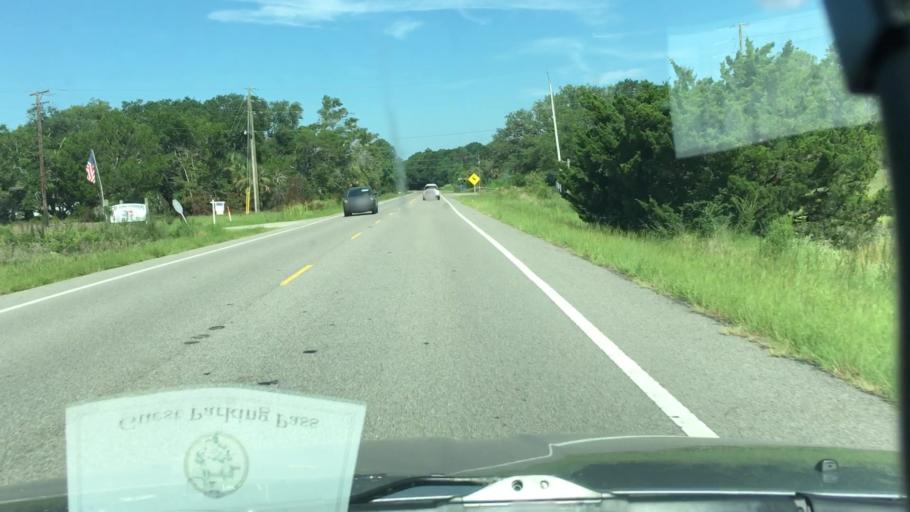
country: US
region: South Carolina
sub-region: Beaufort County
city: Beaufort
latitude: 32.4129
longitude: -80.4776
